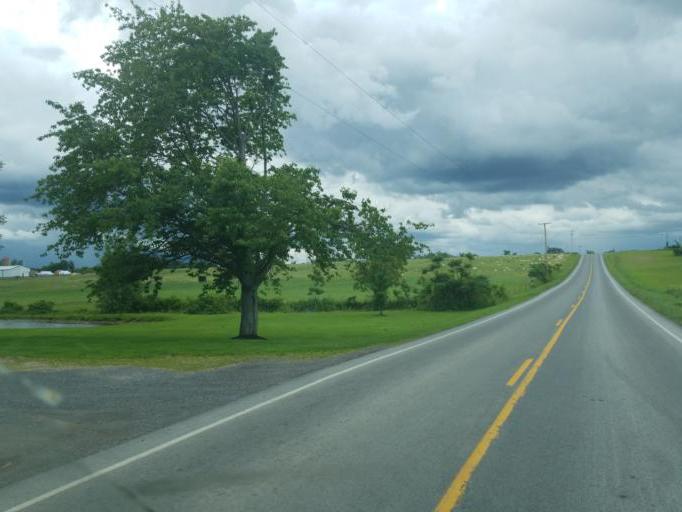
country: US
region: New York
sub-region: Wayne County
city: Lyons
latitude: 43.0249
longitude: -76.9234
